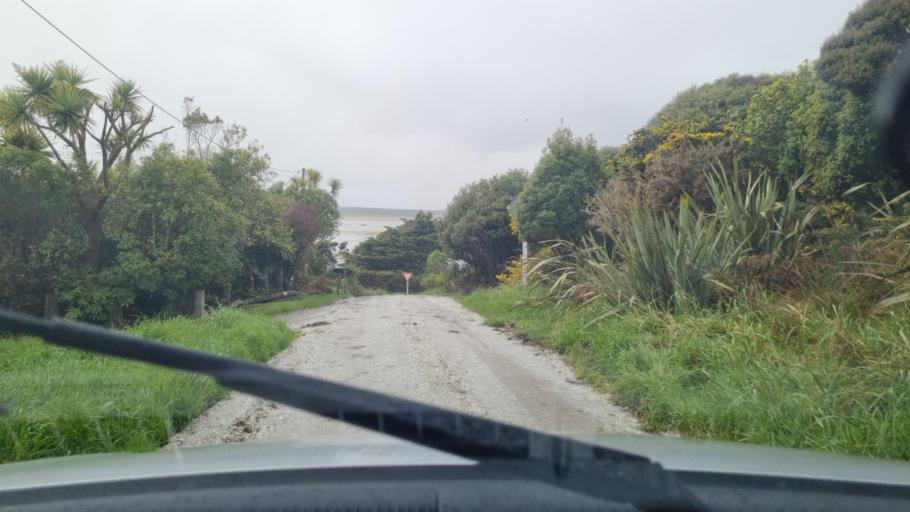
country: NZ
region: Southland
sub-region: Invercargill City
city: Bluff
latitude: -46.5184
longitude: 168.2590
